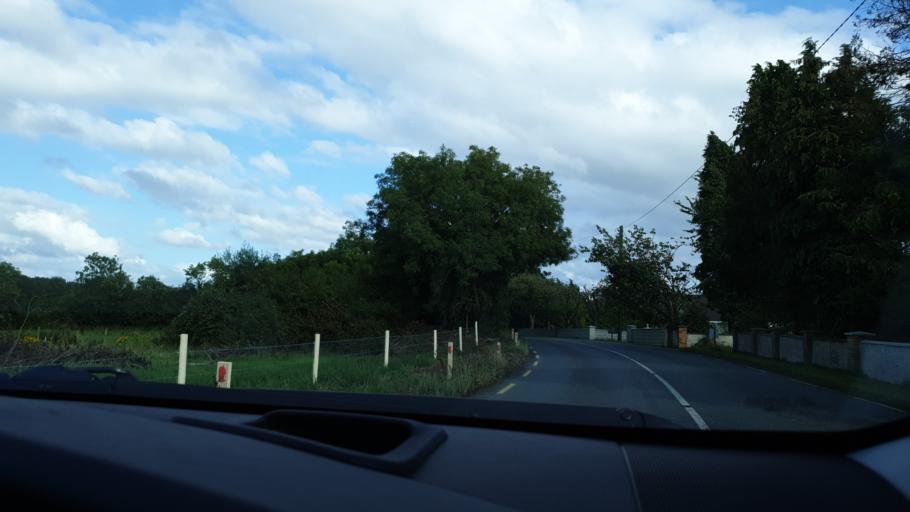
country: IE
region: Leinster
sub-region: An Mhi
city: Ashbourne
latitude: 53.4960
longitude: -6.3991
